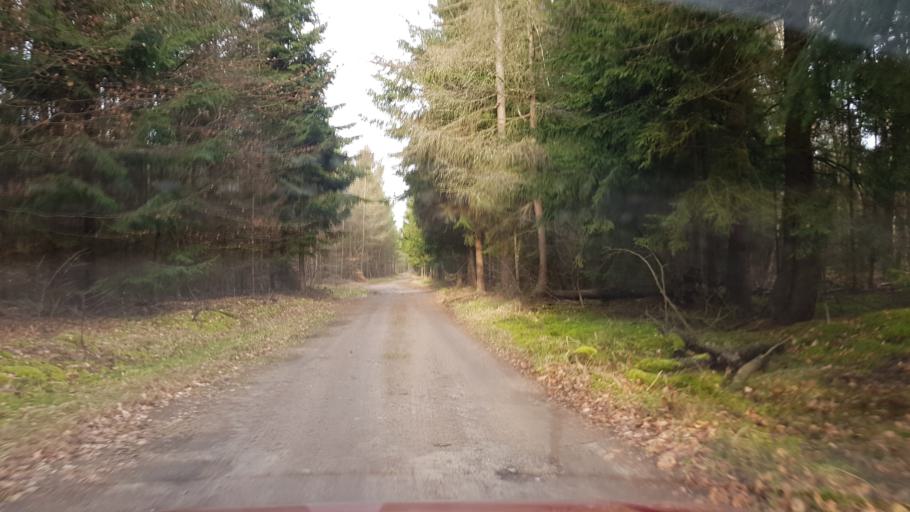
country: PL
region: Lubusz
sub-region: Powiat strzelecko-drezdenecki
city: Strzelce Krajenskie
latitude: 52.9112
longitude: 15.4094
